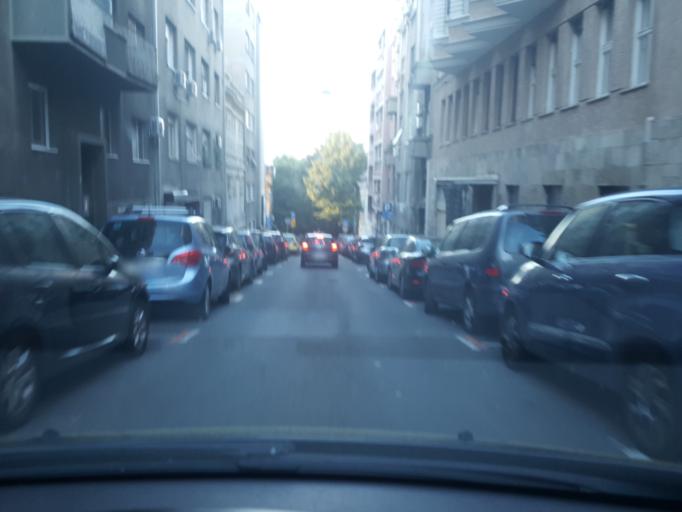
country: RS
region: Central Serbia
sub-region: Belgrade
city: Stari Grad
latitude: 44.8203
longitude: 20.4599
